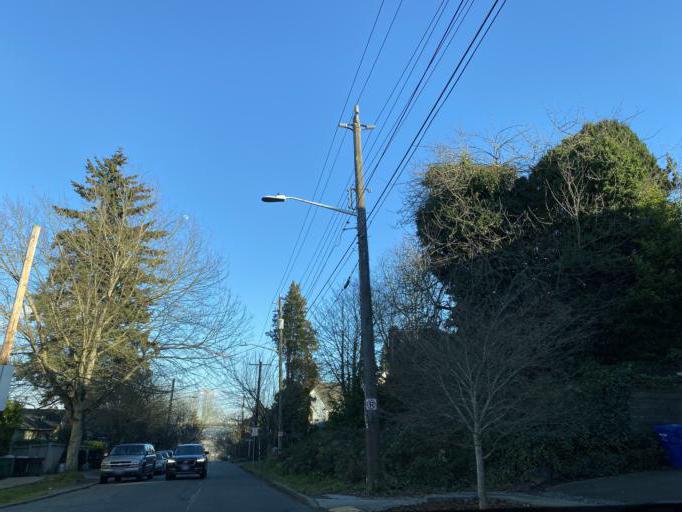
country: US
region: Washington
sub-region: King County
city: Seattle
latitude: 47.6468
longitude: -122.3578
